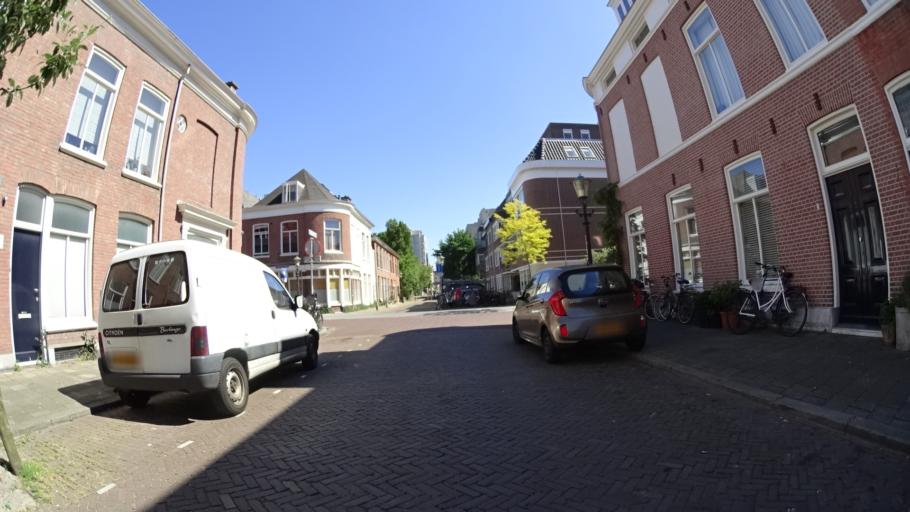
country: NL
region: South Holland
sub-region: Gemeente Den Haag
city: The Hague
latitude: 52.0908
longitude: 4.2994
